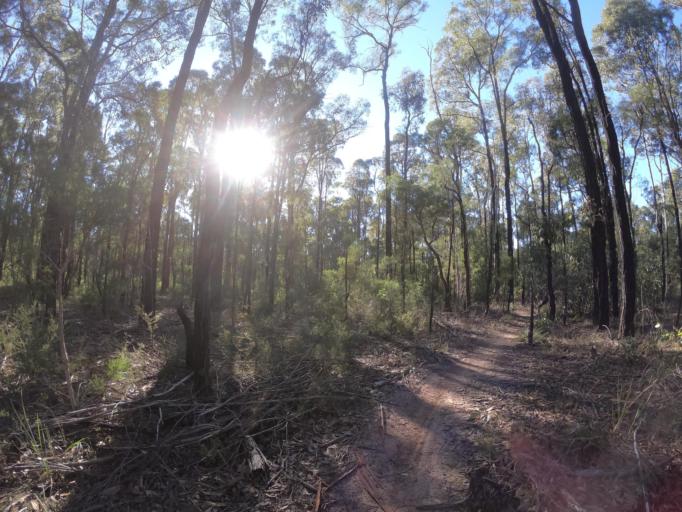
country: AU
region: New South Wales
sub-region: Hawkesbury
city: South Windsor
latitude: -33.6453
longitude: 150.7919
